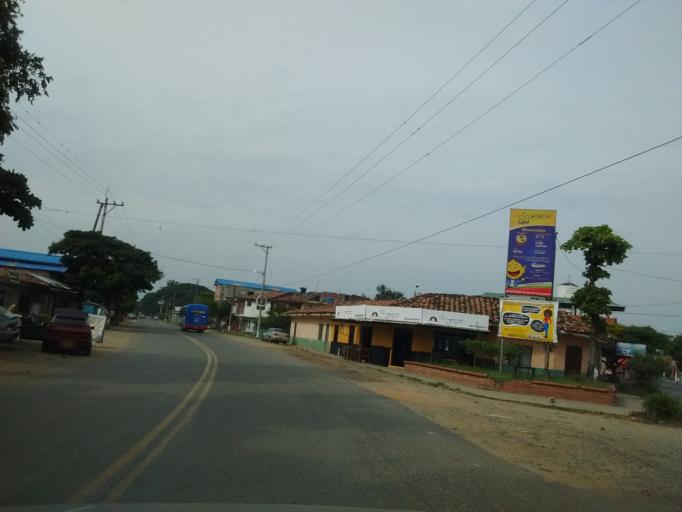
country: CO
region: Cauca
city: Puerto Tejada
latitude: 3.1738
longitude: -76.4579
